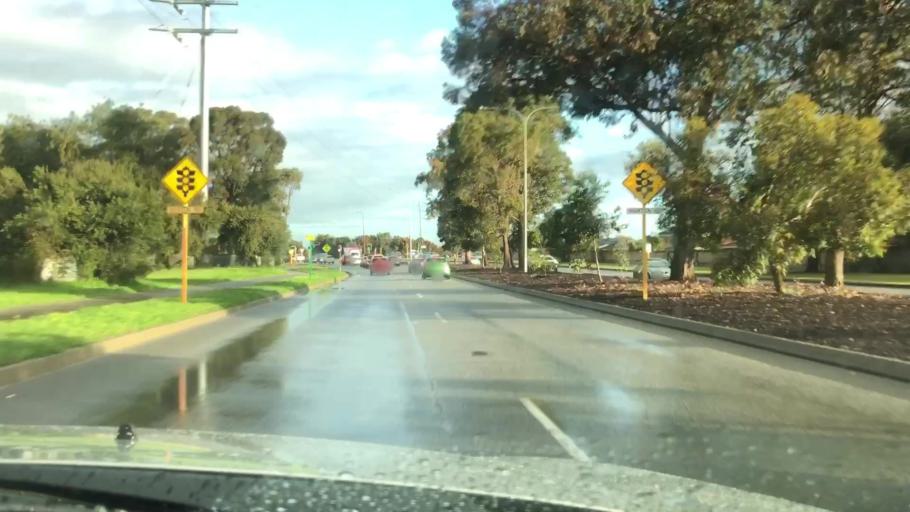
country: AU
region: Western Australia
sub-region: Armadale
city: Harrisdale
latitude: -32.0985
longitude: 115.9305
